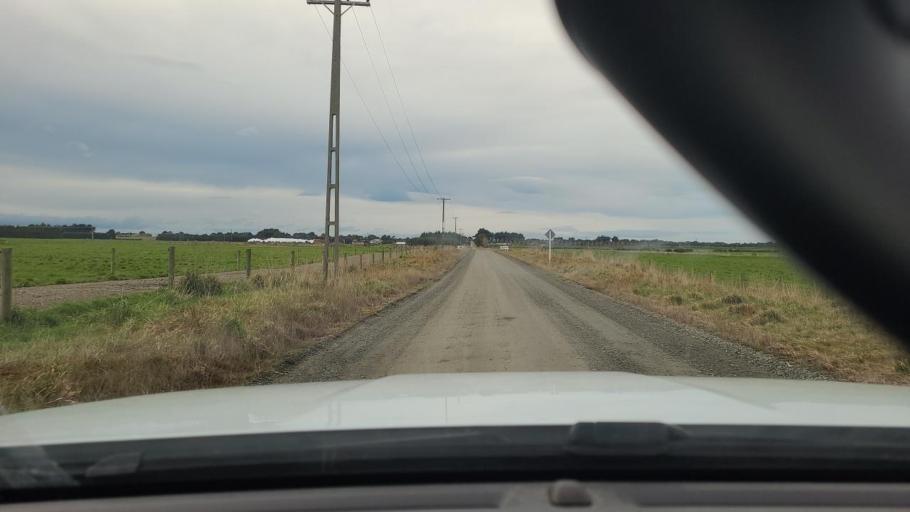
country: NZ
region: Southland
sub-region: Invercargill City
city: Invercargill
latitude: -46.3297
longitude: 168.3149
